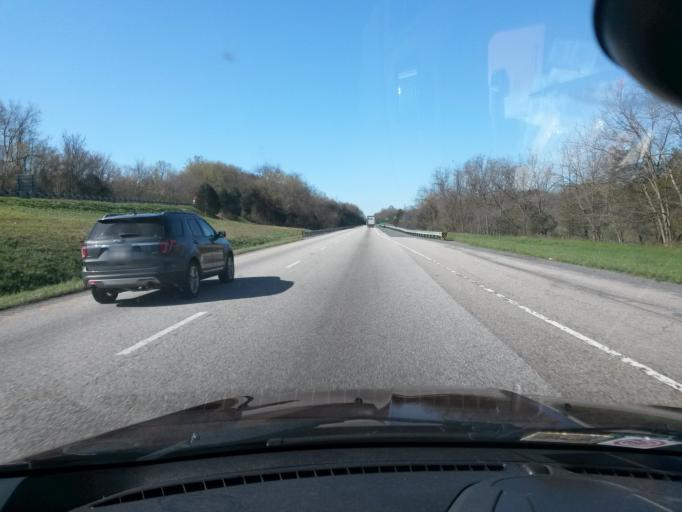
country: US
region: Virginia
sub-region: City of Lexington
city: Lexington
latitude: 37.7501
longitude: -79.4152
